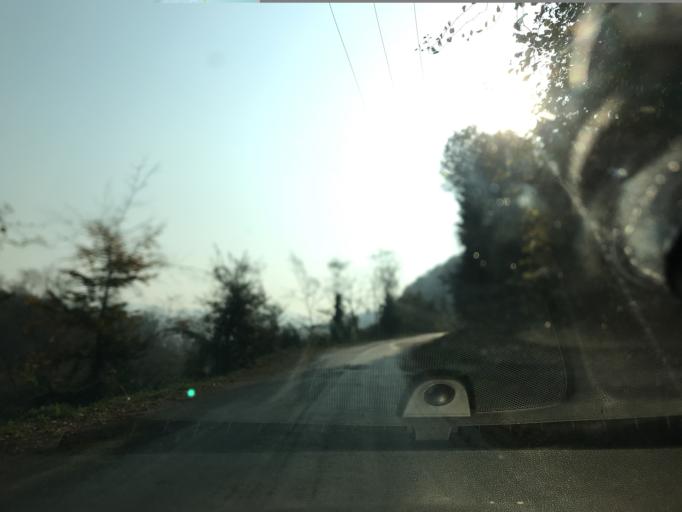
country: TR
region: Duzce
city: Cumayeri
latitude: 40.9167
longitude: 30.9344
